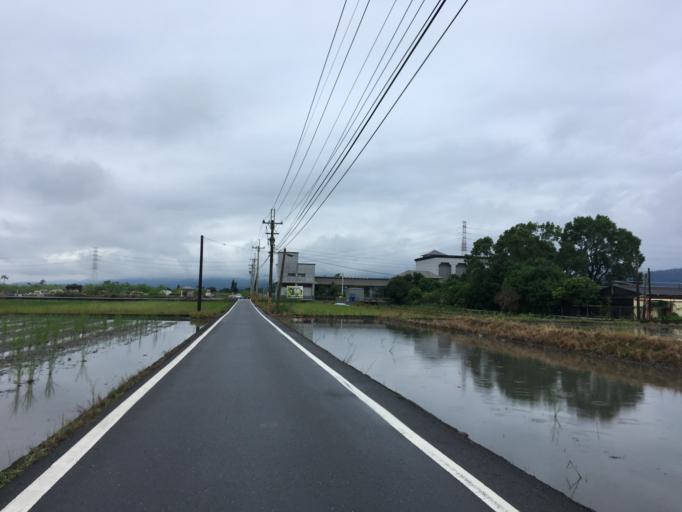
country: TW
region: Taiwan
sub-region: Yilan
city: Yilan
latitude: 24.6643
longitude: 121.7449
